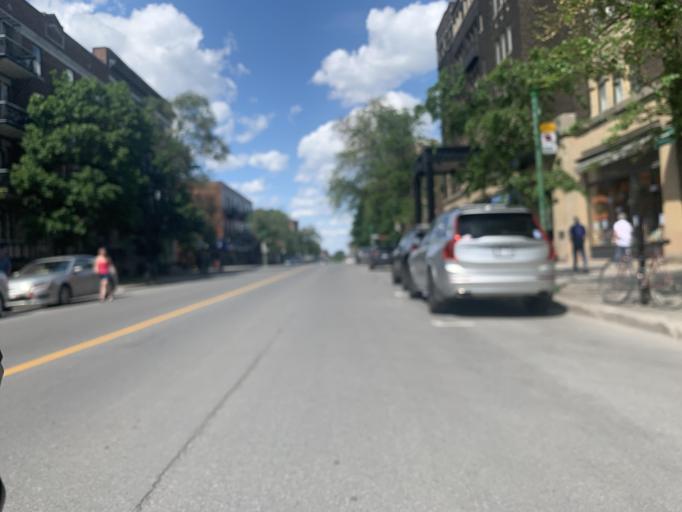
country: CA
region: Quebec
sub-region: Montreal
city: Montreal
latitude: 45.5212
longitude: -73.6077
